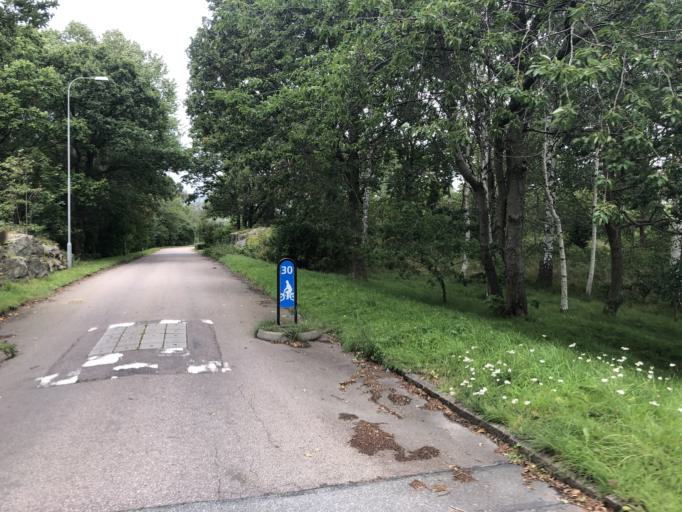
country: SE
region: Vaestra Goetaland
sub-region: Goteborg
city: Goeteborg
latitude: 57.7646
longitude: 11.9442
